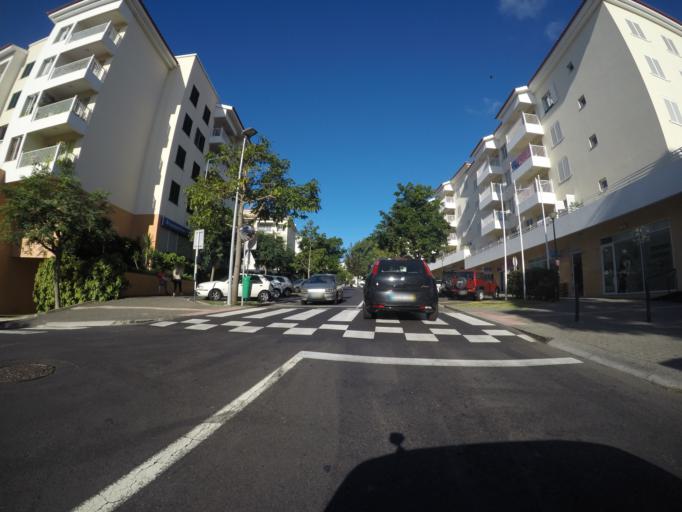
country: PT
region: Madeira
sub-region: Funchal
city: Nossa Senhora do Monte
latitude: 32.6603
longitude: -16.9300
